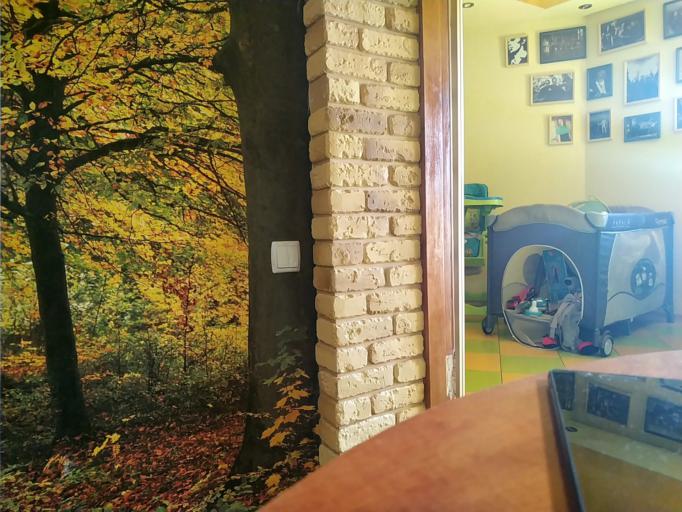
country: RU
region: Tverskaya
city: Vyshniy Volochek
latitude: 57.5830
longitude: 34.5725
